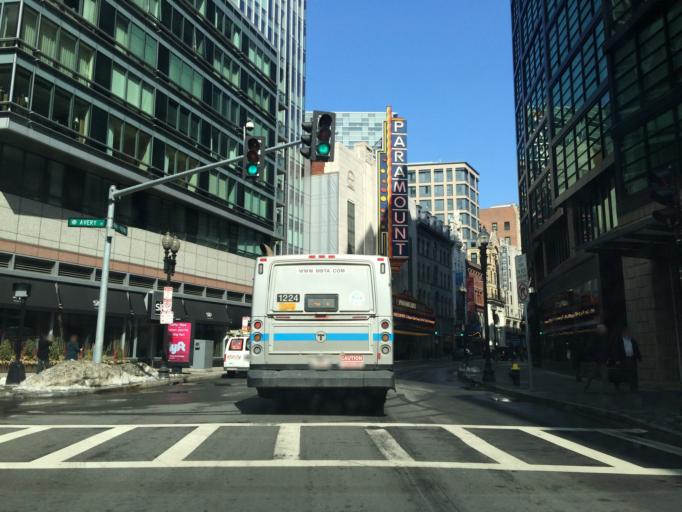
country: US
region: Massachusetts
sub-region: Suffolk County
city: Boston
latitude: 42.3531
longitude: -71.0626
